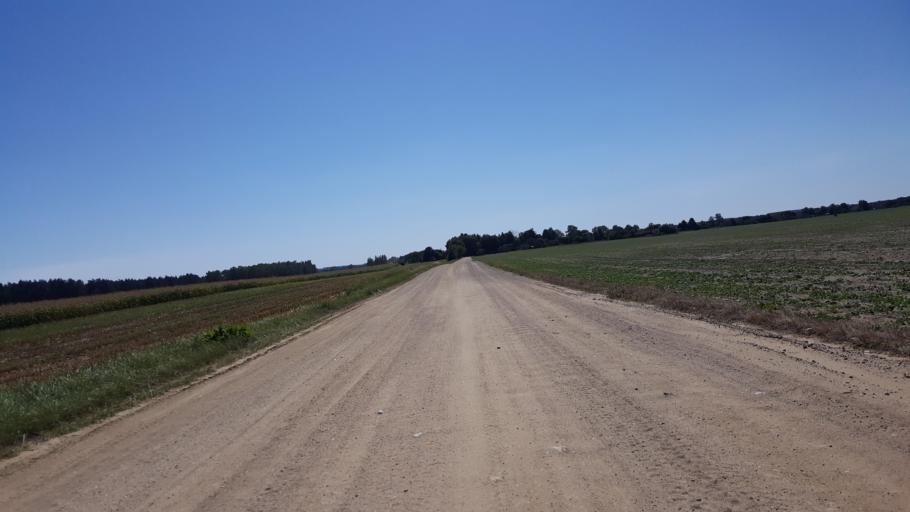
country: PL
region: Lublin Voivodeship
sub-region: Powiat bialski
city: Rokitno
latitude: 52.2200
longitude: 23.3981
